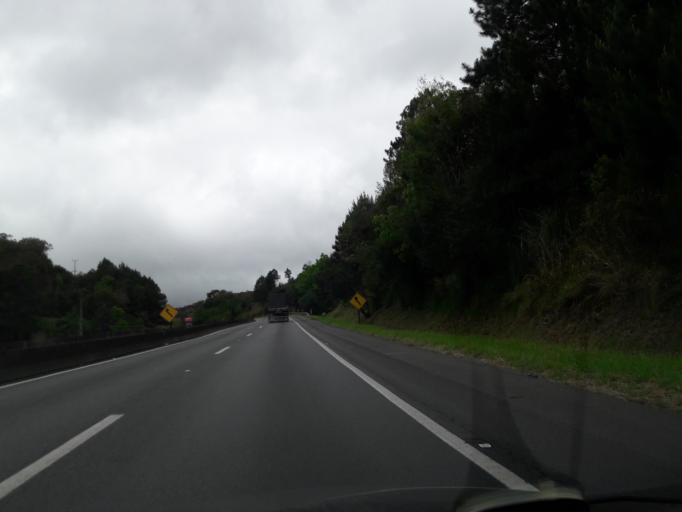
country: BR
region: Parana
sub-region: Campina Grande Do Sul
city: Campina Grande do Sul
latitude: -25.2082
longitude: -48.8962
